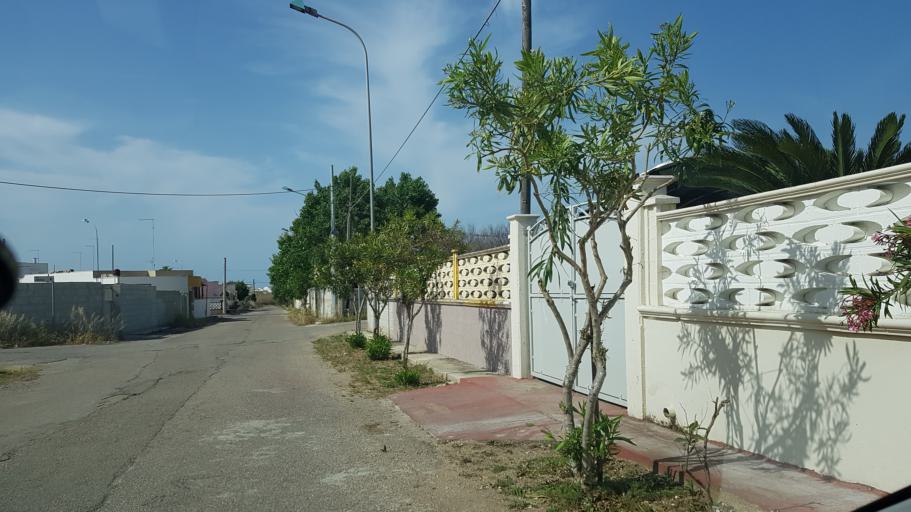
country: IT
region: Apulia
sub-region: Provincia di Brindisi
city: Torchiarolo
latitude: 40.5290
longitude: 18.0754
